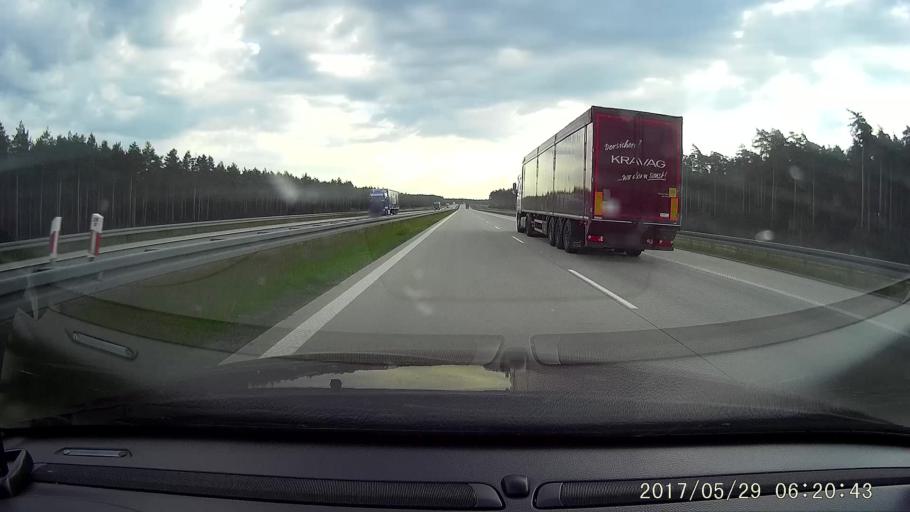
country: PL
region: Lower Silesian Voivodeship
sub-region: Powiat boleslawiecki
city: Boleslawiec
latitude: 51.2954
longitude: 15.4981
